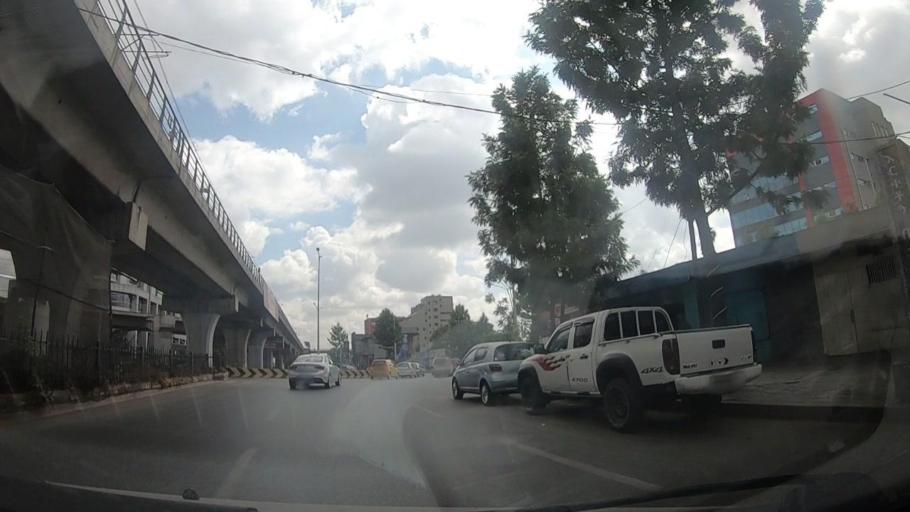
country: ET
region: Adis Abeba
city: Addis Ababa
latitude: 9.0115
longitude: 38.7337
